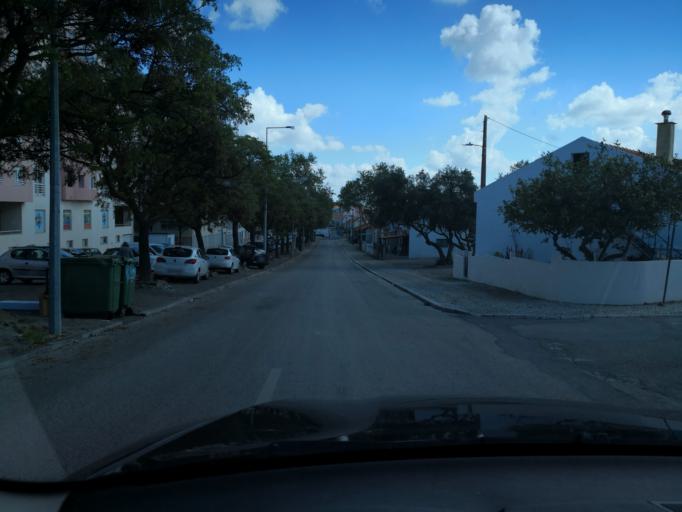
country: PT
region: Setubal
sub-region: Setubal
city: Setubal
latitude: 38.5222
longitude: -8.8648
